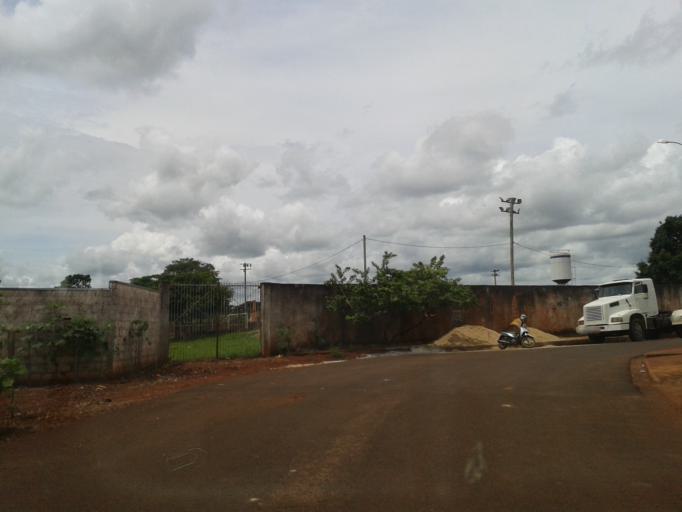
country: BR
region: Minas Gerais
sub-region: Centralina
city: Centralina
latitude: -18.5791
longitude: -49.2044
